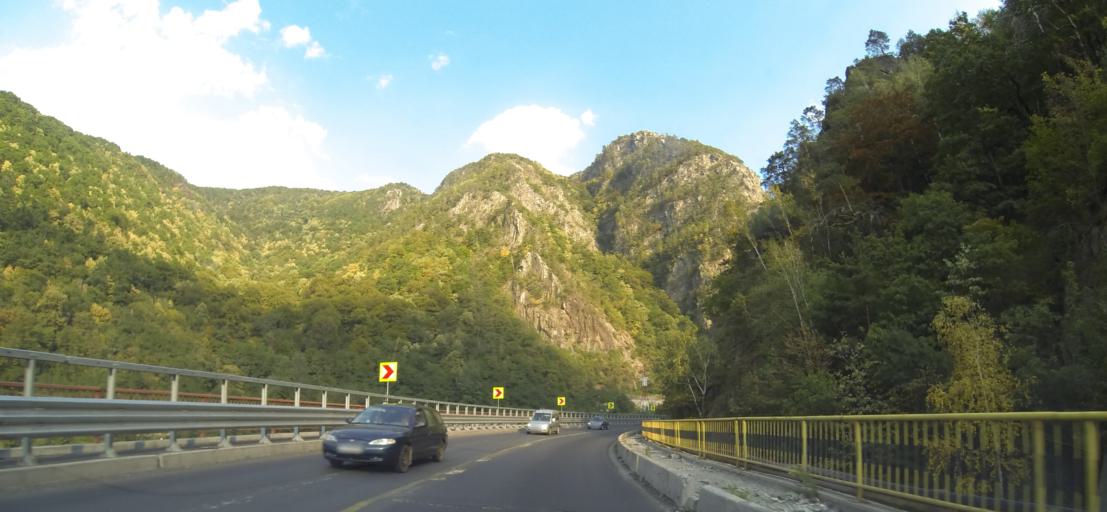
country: RO
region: Valcea
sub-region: Comuna Brezoi
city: Brezoi
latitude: 45.2988
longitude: 24.2894
